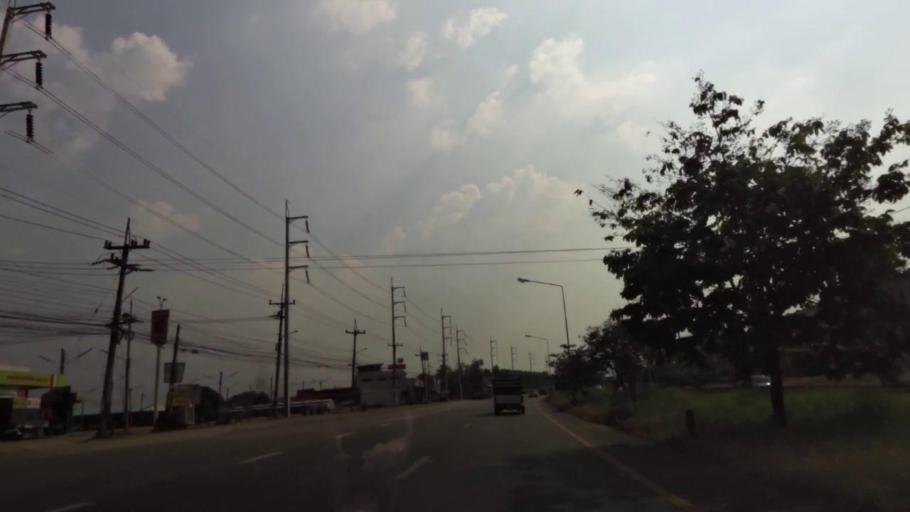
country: TH
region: Chon Buri
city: Nong Yai
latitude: 13.2057
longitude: 101.2452
